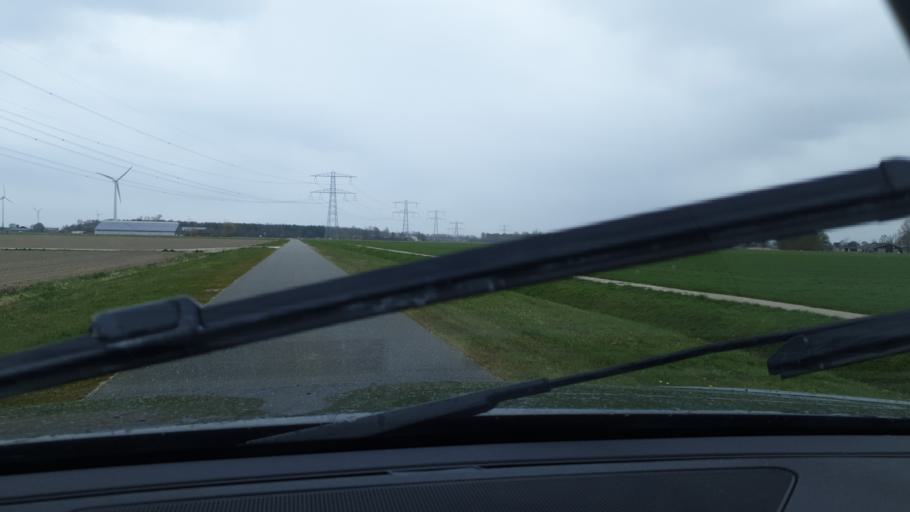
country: NL
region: Flevoland
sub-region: Gemeente Urk
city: Urk
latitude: 52.5782
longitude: 5.5584
